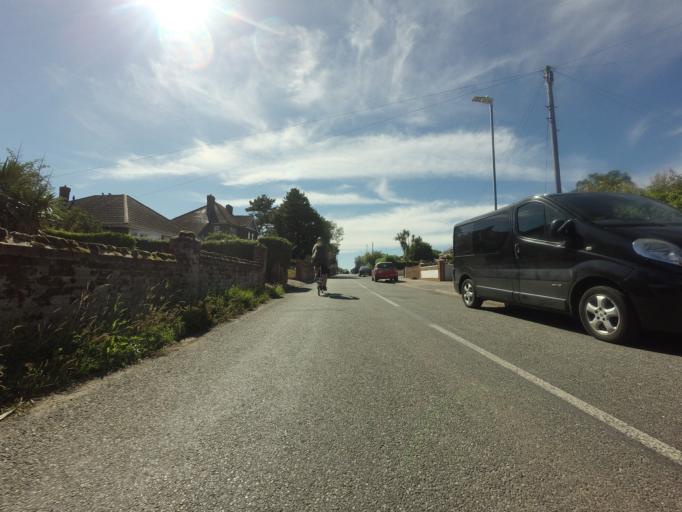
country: GB
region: England
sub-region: Kent
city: Birchington-on-Sea
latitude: 51.3354
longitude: 1.3061
